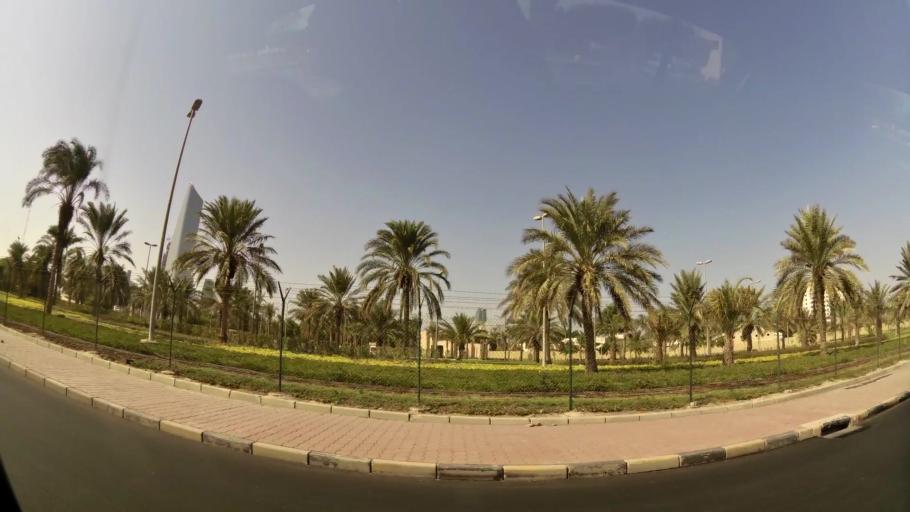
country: KW
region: Al Asimah
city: Ad Dasmah
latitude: 29.3865
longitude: 48.0021
